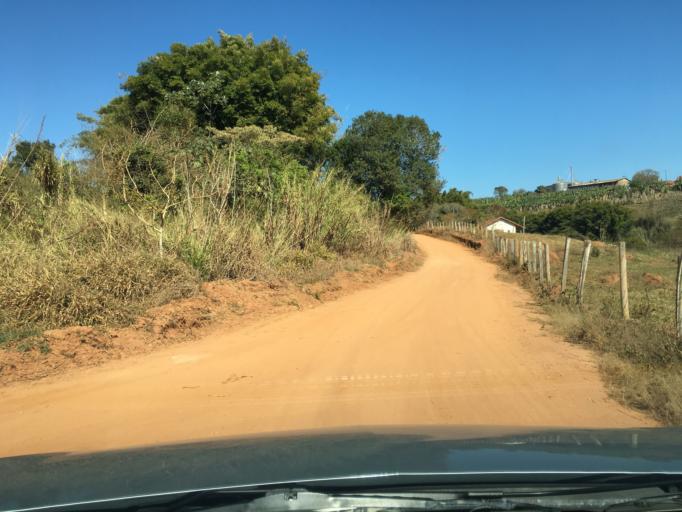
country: BR
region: Minas Gerais
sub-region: Campestre
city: Campestre
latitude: -21.5697
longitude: -46.1981
